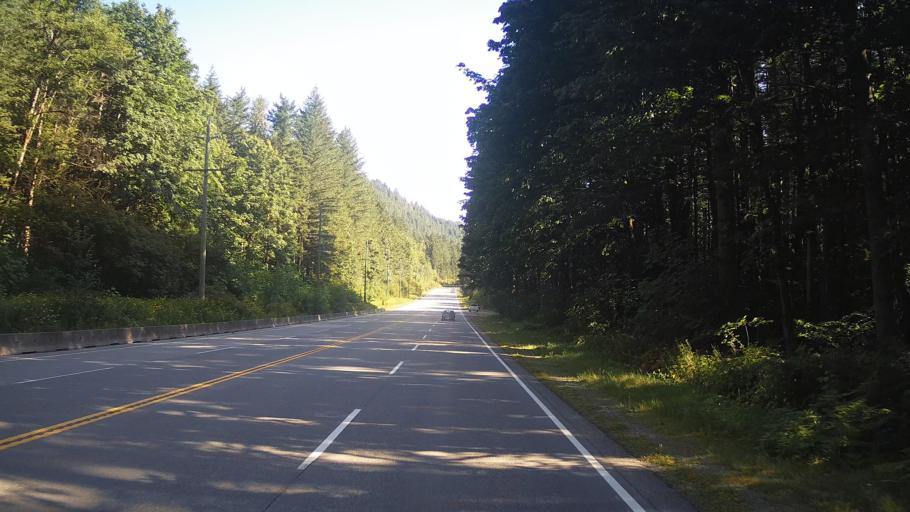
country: CA
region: British Columbia
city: Hope
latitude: 49.4556
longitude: -121.4363
